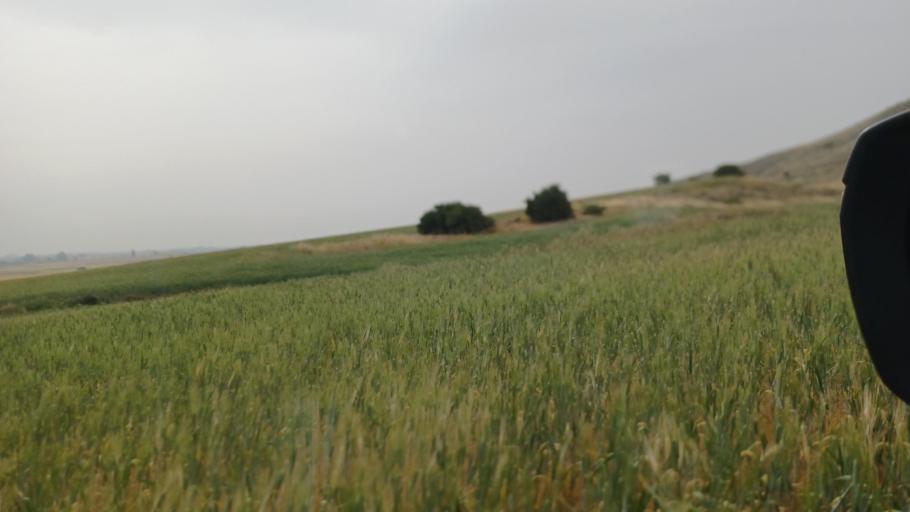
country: CY
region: Lefkosia
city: Mammari
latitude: 35.1675
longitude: 33.2336
